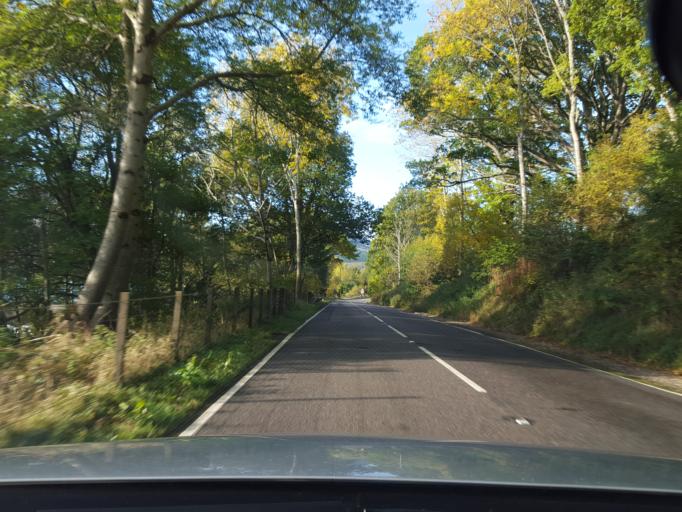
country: GB
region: Scotland
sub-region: Highland
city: Beauly
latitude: 57.3371
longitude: -4.4423
